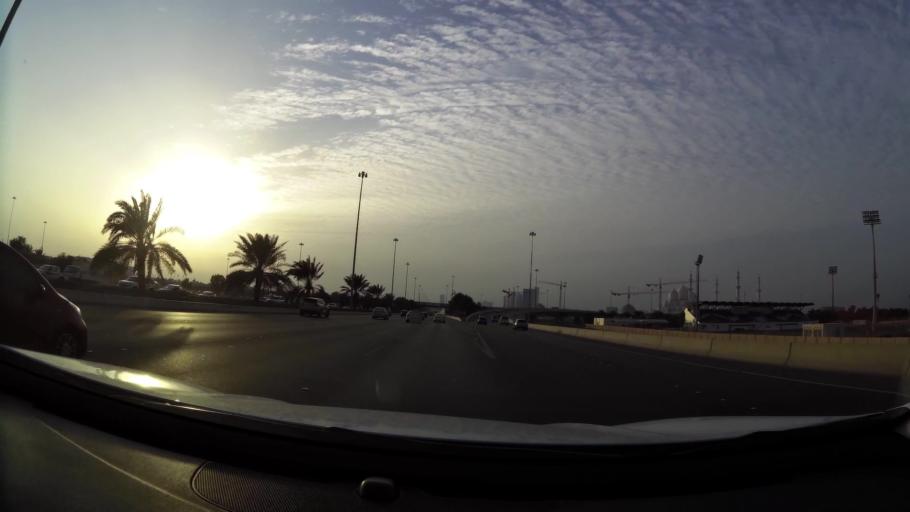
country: AE
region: Abu Dhabi
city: Abu Dhabi
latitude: 24.4050
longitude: 54.4812
